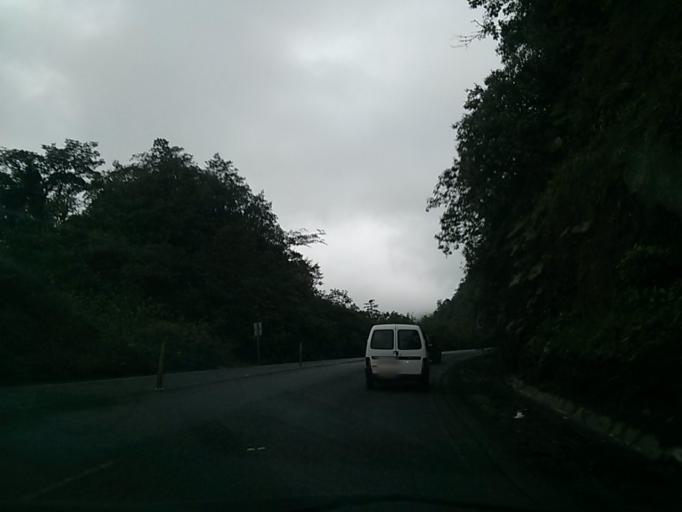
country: CR
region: San Jose
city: Dulce Nombre de Jesus
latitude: 10.0679
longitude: -83.9881
